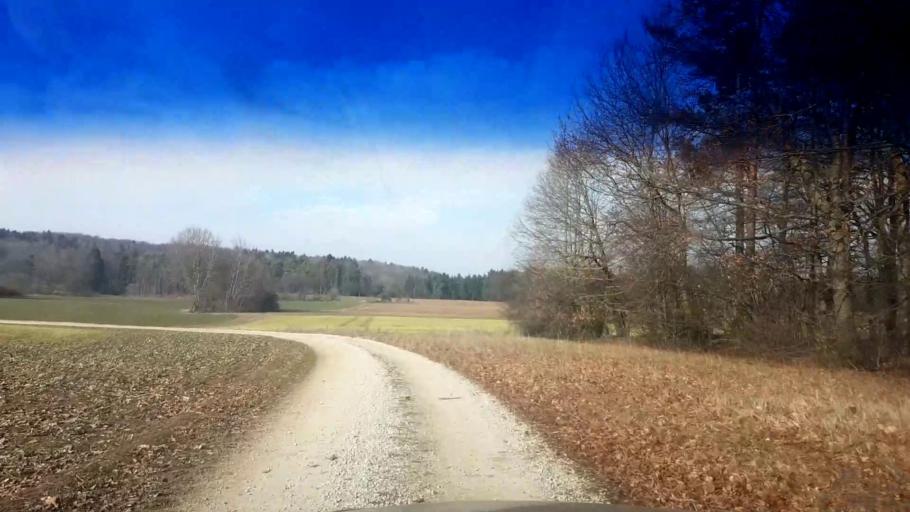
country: DE
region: Bavaria
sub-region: Upper Franconia
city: Poxdorf
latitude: 49.9290
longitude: 11.0665
